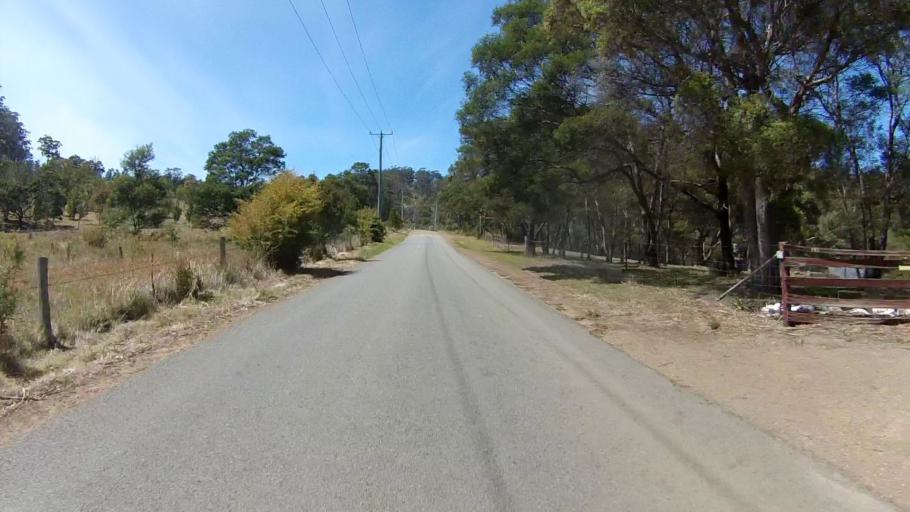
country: AU
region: Tasmania
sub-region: Sorell
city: Sorell
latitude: -42.7659
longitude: 147.6503
